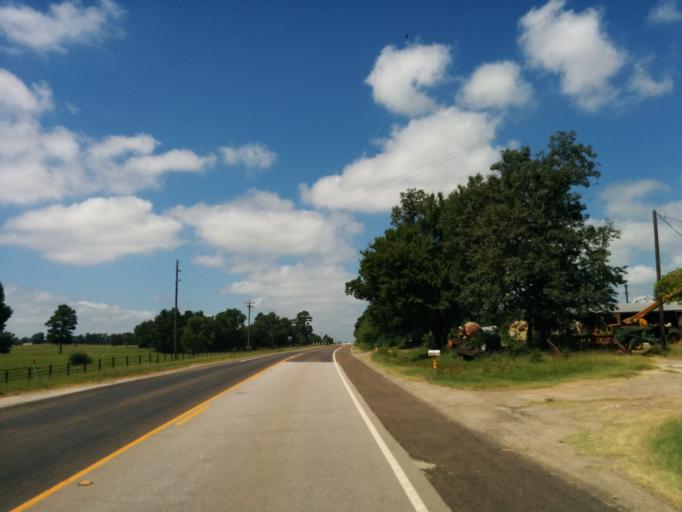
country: US
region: Texas
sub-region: Houston County
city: Crockett
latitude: 31.2993
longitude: -95.4926
